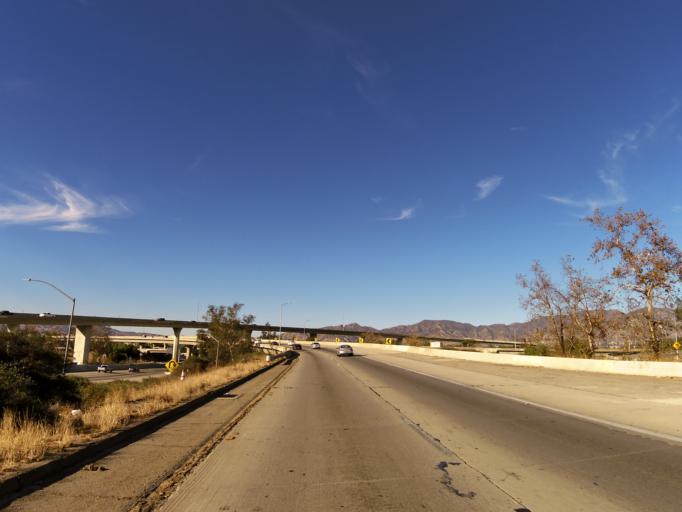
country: US
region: California
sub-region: Los Angeles County
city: San Fernando
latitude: 34.2640
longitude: -118.4410
